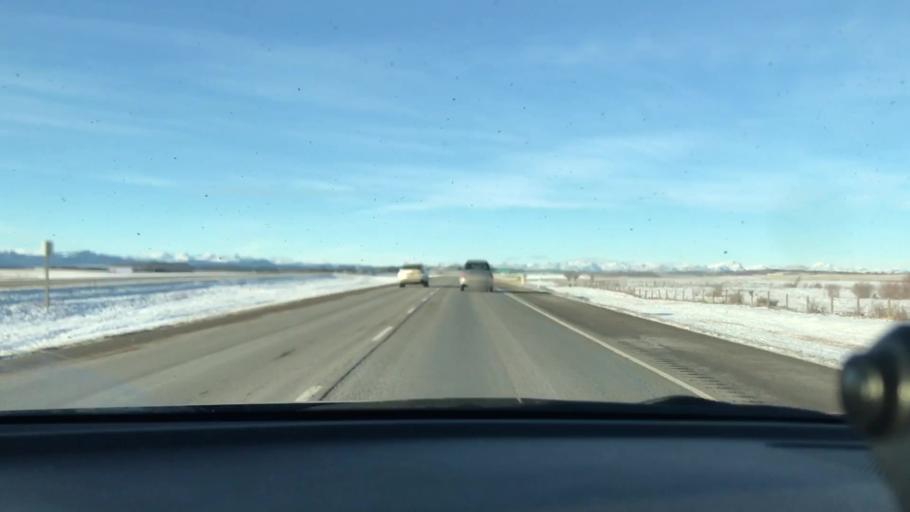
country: CA
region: Alberta
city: Cochrane
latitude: 51.0877
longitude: -114.5193
